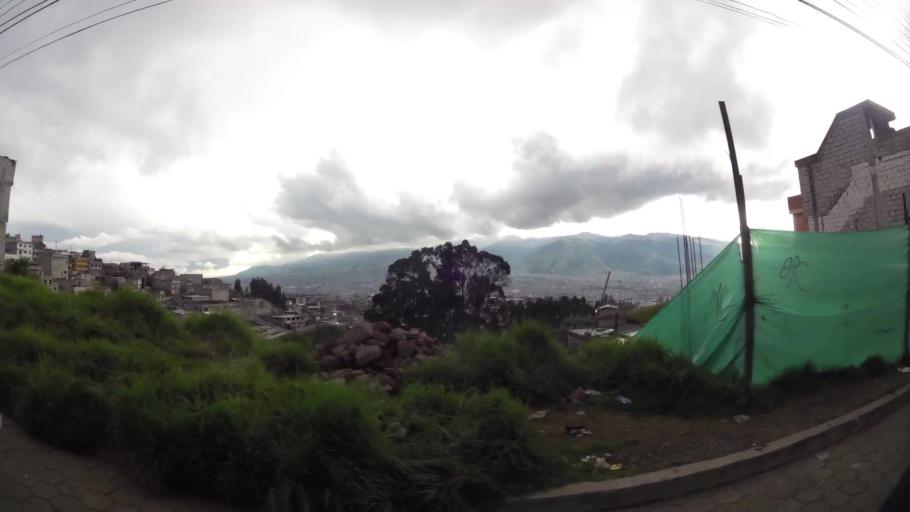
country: EC
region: Pichincha
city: Quito
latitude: -0.3030
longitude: -78.5223
